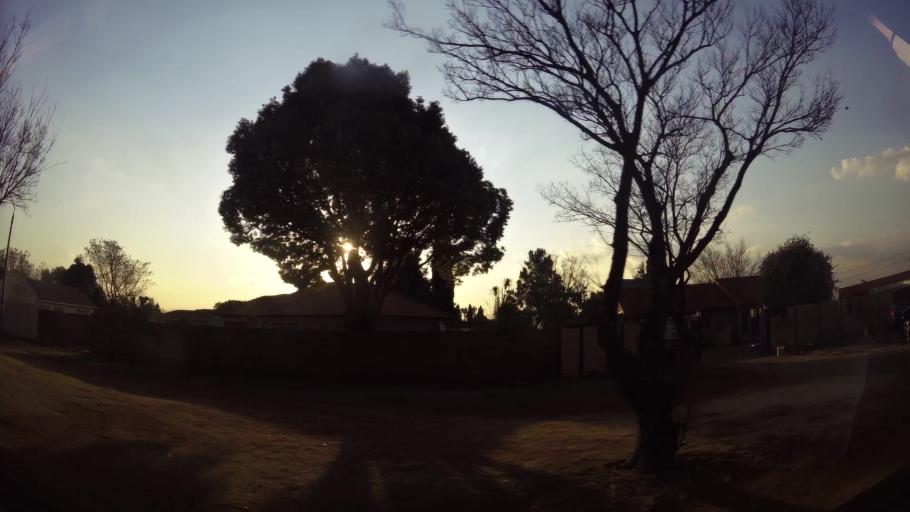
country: ZA
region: Gauteng
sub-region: Ekurhuleni Metropolitan Municipality
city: Boksburg
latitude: -26.2968
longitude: 28.2503
